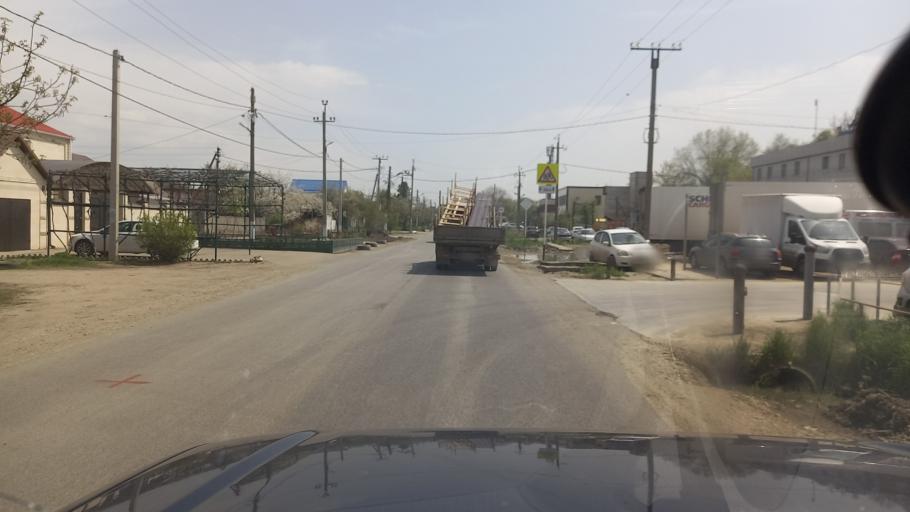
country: RU
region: Adygeya
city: Yablonovskiy
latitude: 44.9880
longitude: 38.9577
